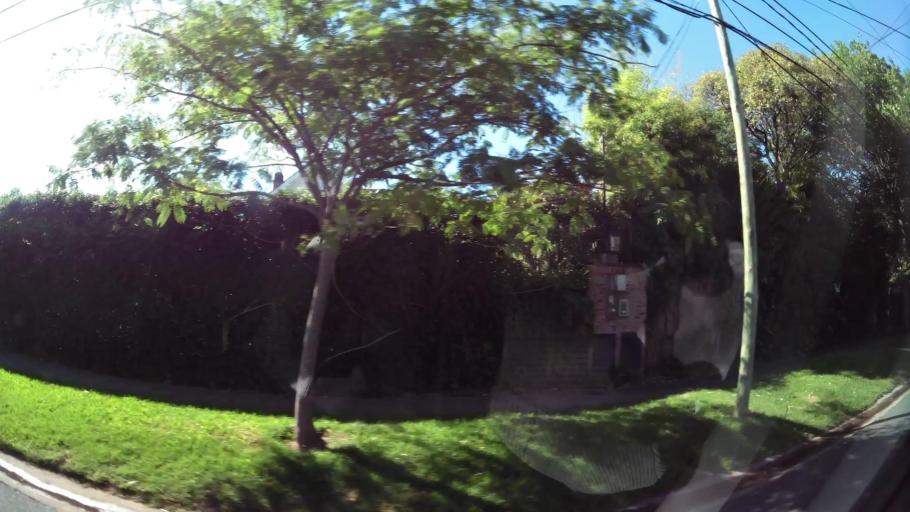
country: AR
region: Buenos Aires
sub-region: Partido de Tigre
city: Tigre
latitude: -34.4840
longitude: -58.5744
